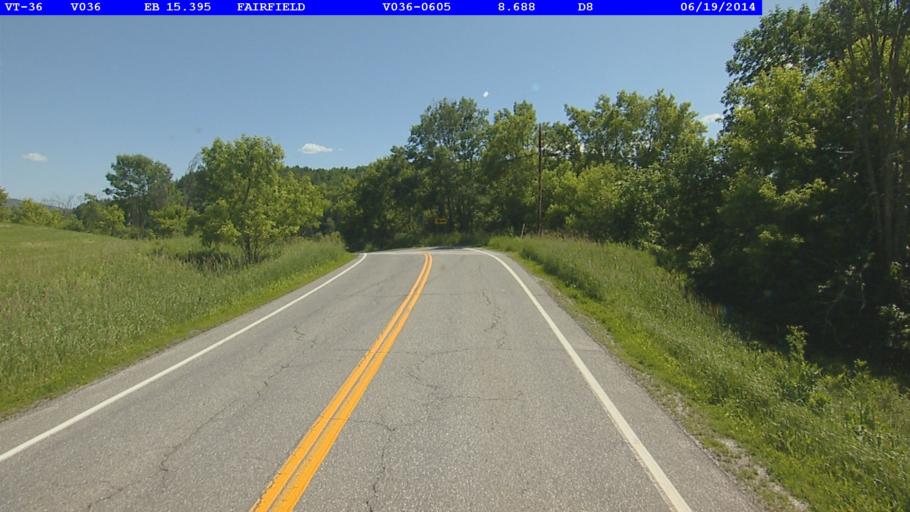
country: US
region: Vermont
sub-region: Franklin County
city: Enosburg Falls
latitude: 44.7919
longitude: -72.8704
